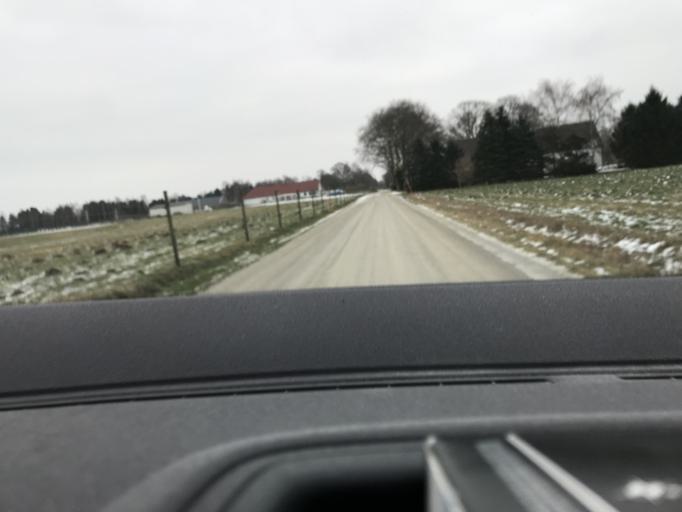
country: SE
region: Skane
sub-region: Ystads Kommun
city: Ystad
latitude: 55.4549
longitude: 13.8669
